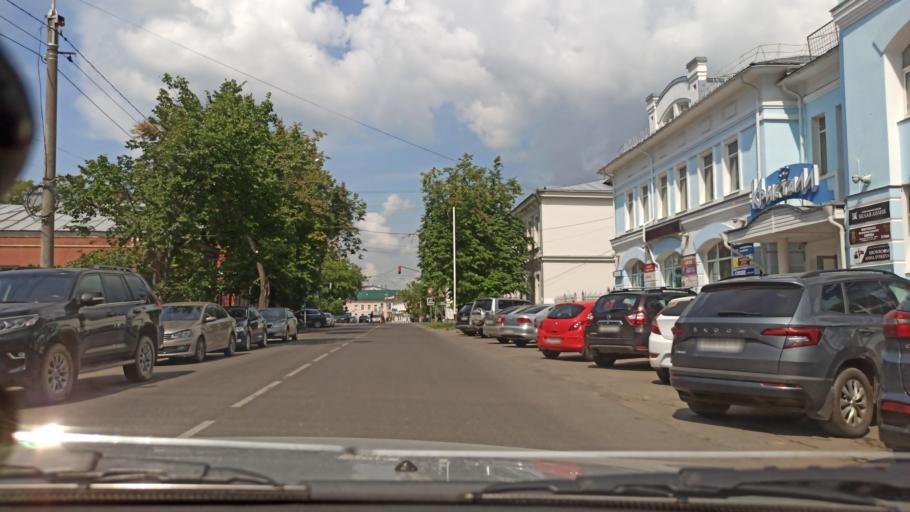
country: RU
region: Vologda
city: Vologda
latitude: 59.2180
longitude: 39.8891
